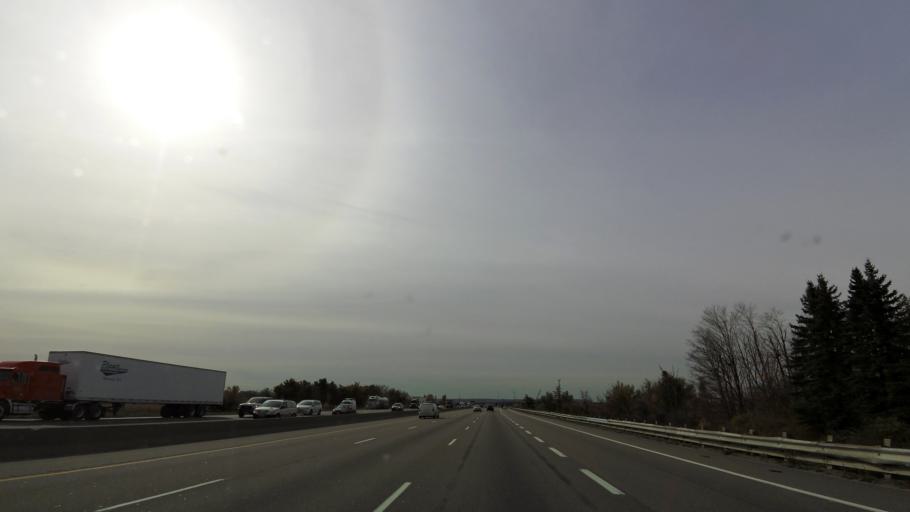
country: CA
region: Ontario
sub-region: Halton
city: Milton
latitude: 43.5766
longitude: -79.8234
